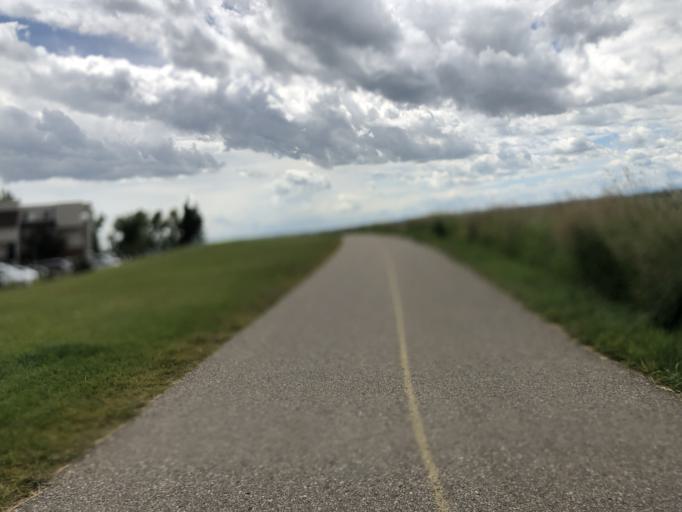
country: CA
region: Alberta
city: Calgary
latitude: 50.9960
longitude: -114.0230
